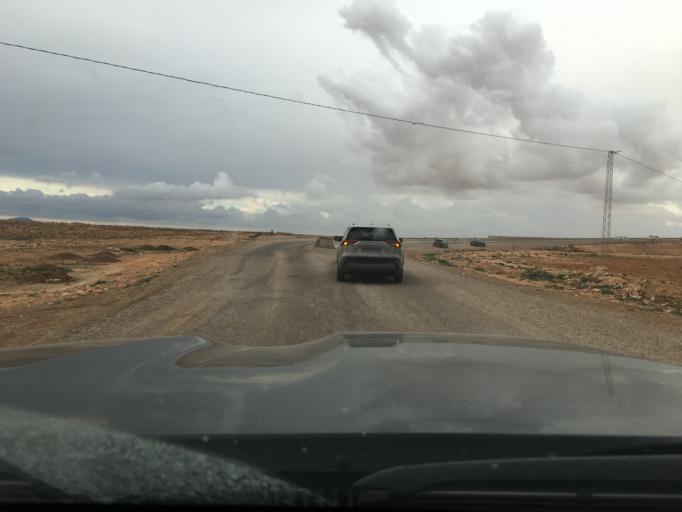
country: TN
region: Madanin
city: Medenine
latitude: 33.2968
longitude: 10.6090
